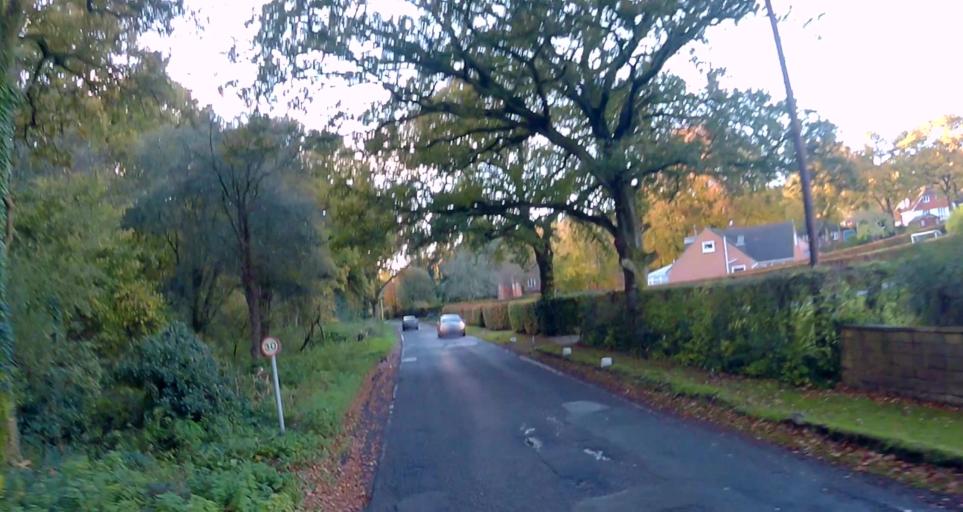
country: GB
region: England
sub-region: Hampshire
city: Basingstoke
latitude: 51.1915
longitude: -1.0910
